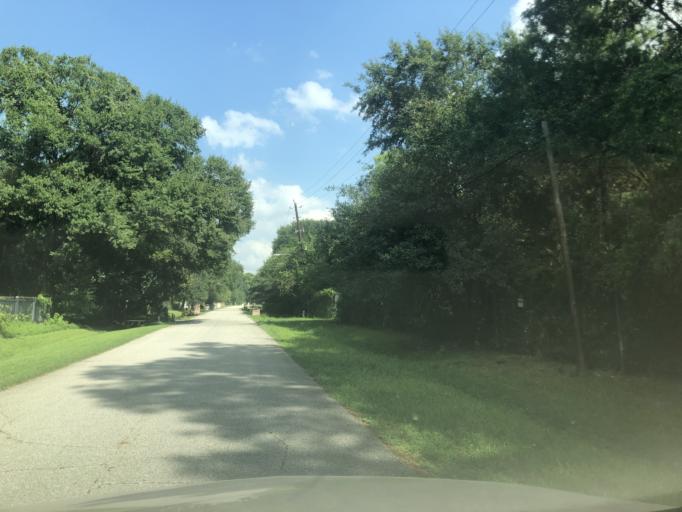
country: US
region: Texas
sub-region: Harris County
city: Bunker Hill Village
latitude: 29.7388
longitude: -95.5415
